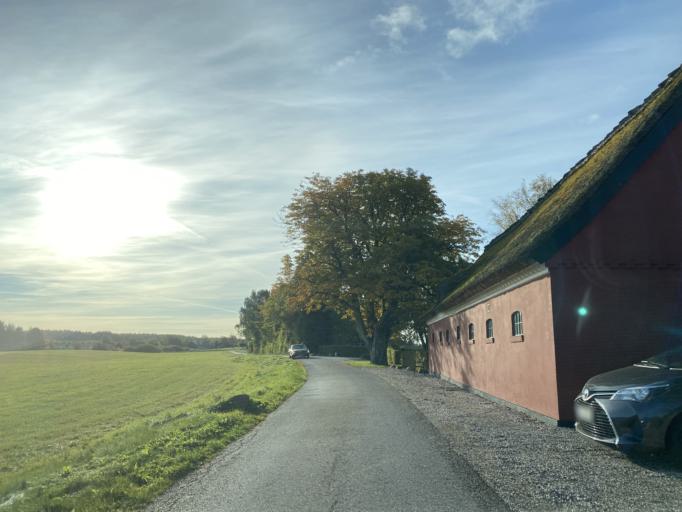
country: DK
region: Capital Region
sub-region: Allerod Kommune
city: Lynge
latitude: 55.8165
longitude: 12.2840
